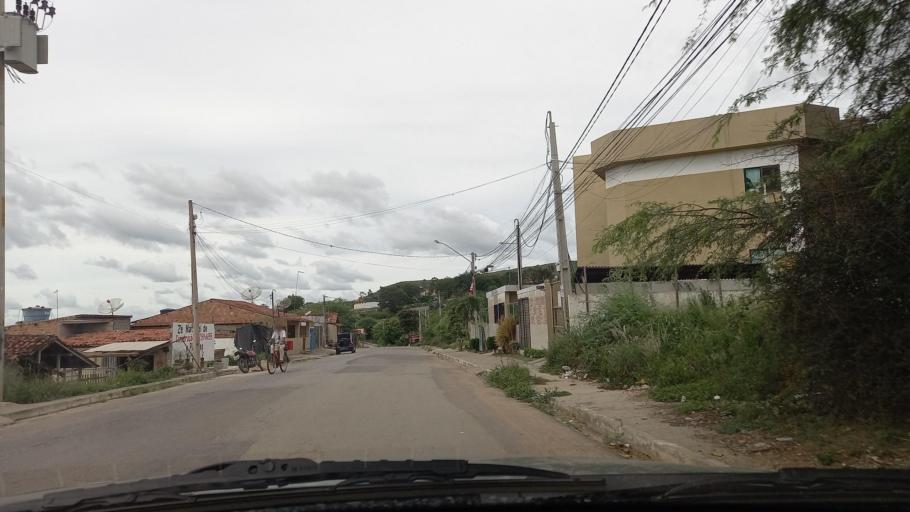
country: BR
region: Pernambuco
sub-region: Gravata
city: Gravata
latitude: -8.2142
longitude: -35.6076
